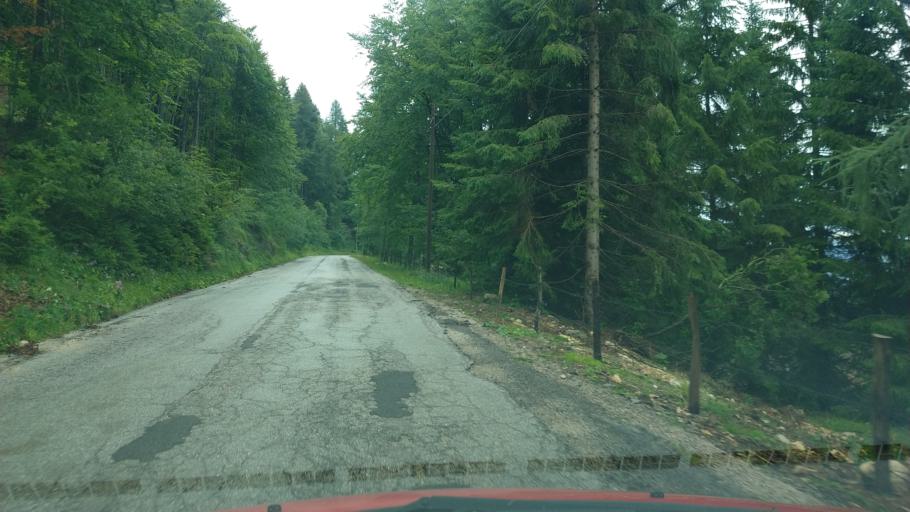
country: IT
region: Veneto
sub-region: Provincia di Vicenza
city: Pedemonte
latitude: 45.8833
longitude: 11.2934
